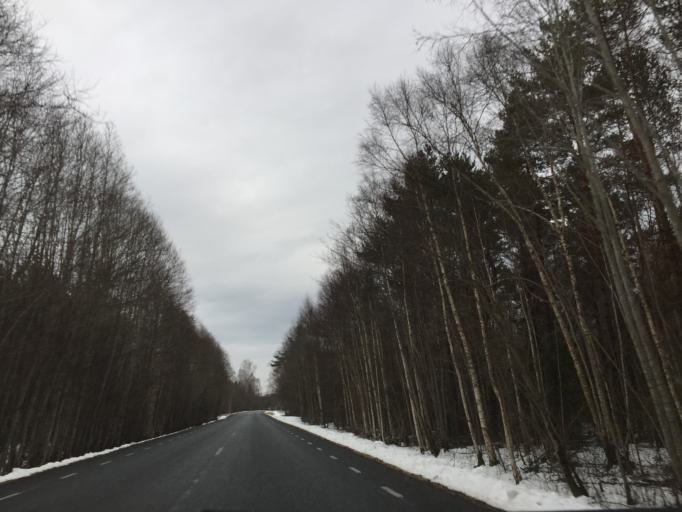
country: EE
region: Saare
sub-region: Orissaare vald
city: Orissaare
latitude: 58.5622
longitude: 22.7712
